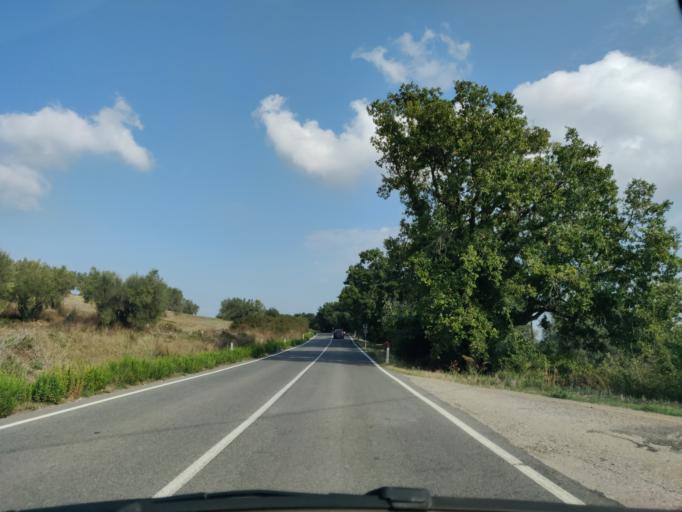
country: IT
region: Latium
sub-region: Provincia di Viterbo
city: Monte Romano
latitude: 42.2635
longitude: 11.8674
